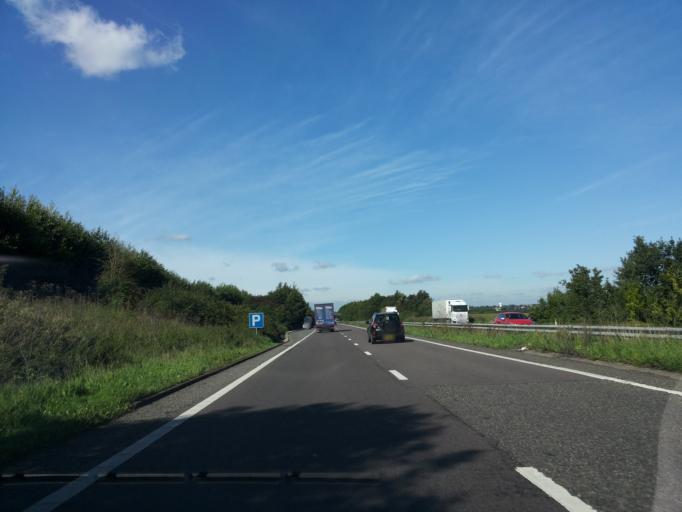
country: GB
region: England
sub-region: Kent
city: Canterbury
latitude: 51.2587
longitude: 1.0767
